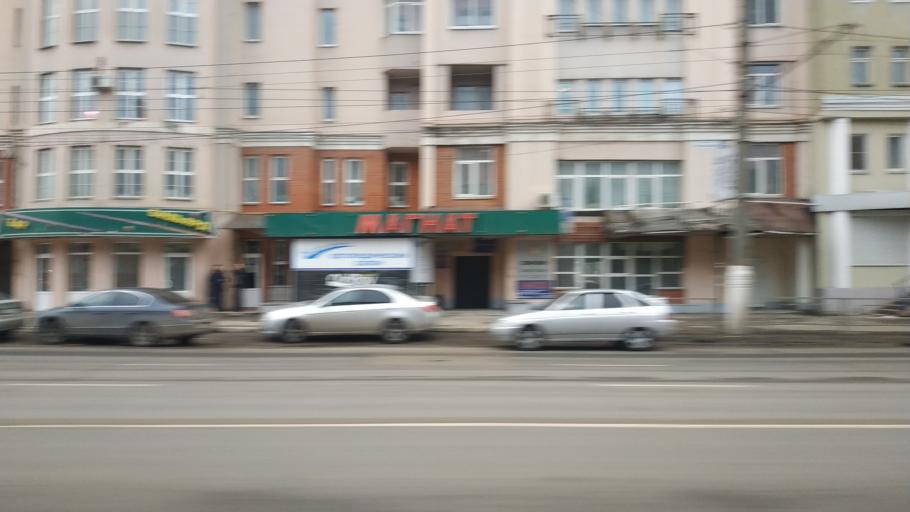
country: RU
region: Tverskaya
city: Tver
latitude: 56.8394
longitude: 35.9120
